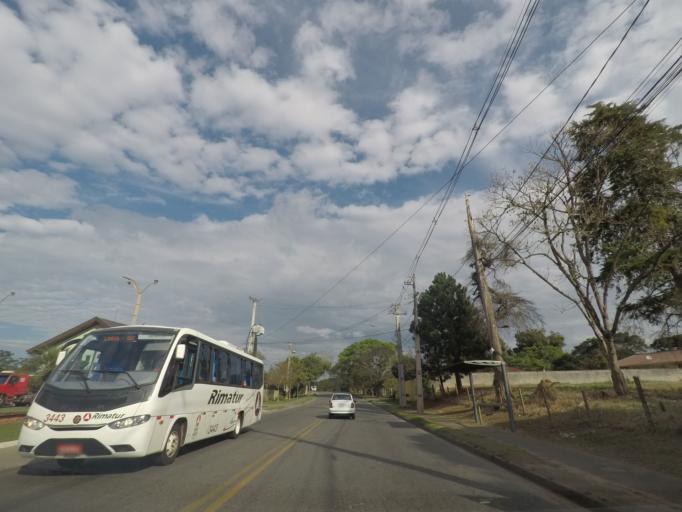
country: BR
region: Parana
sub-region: Sao Jose Dos Pinhais
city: Sao Jose dos Pinhais
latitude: -25.5614
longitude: -49.2913
